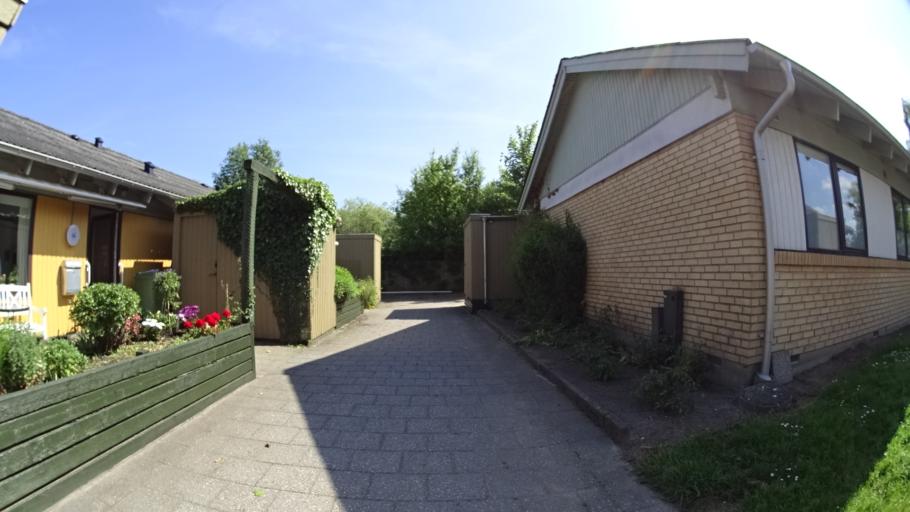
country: DK
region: Central Jutland
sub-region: Arhus Kommune
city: Arhus
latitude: 56.1519
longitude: 10.1638
